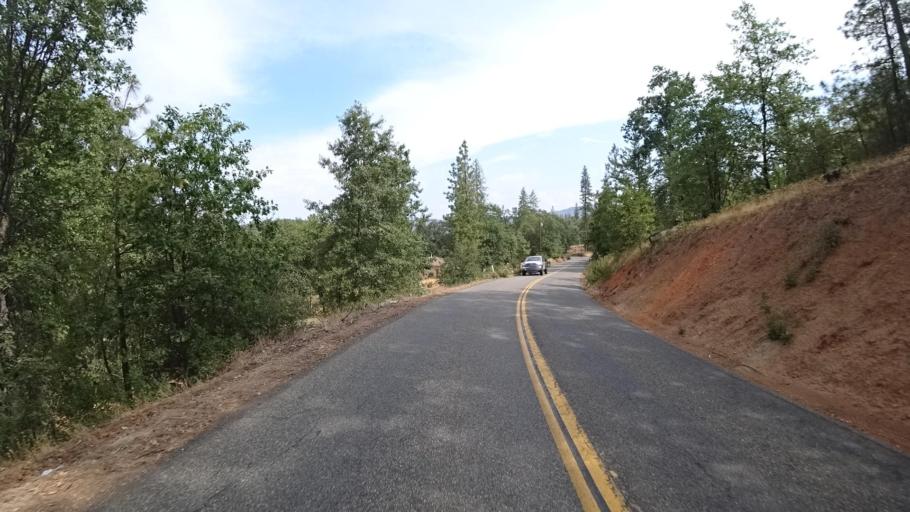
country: US
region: California
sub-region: Mariposa County
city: Midpines
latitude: 37.5179
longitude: -119.9179
